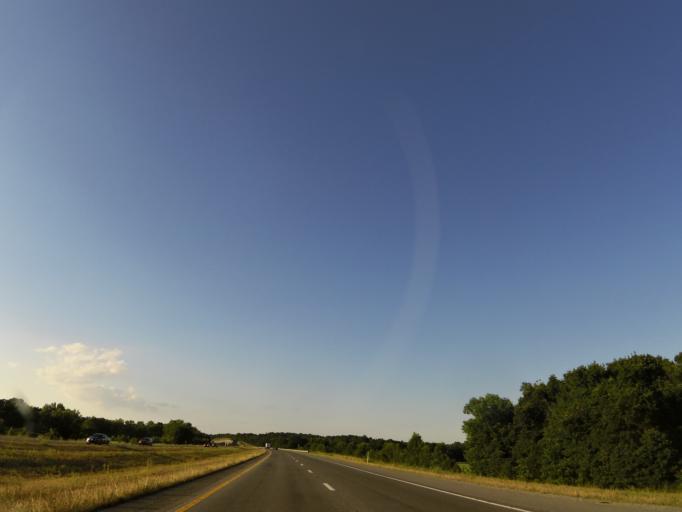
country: US
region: Tennessee
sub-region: Rutherford County
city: Smyrna
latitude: 35.9965
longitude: -86.4313
